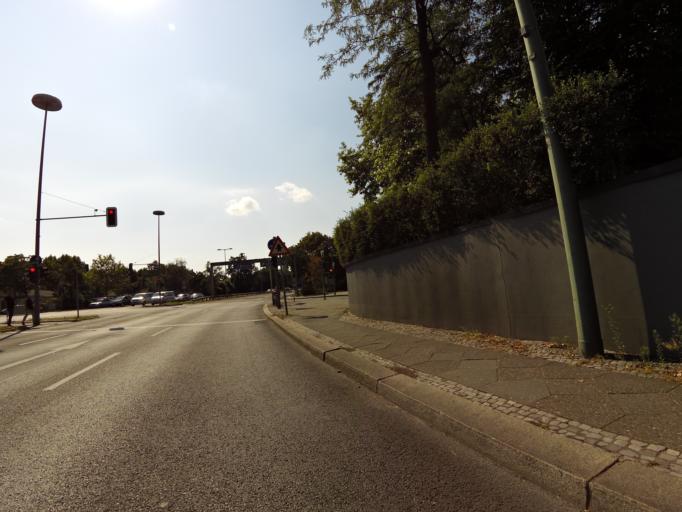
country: DE
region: Berlin
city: Wilmersdorf Bezirk
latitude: 52.4880
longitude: 13.3081
